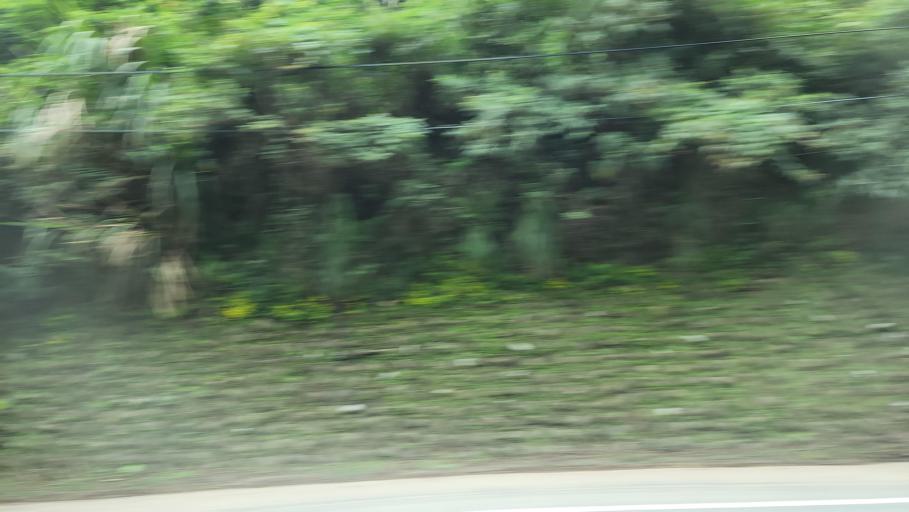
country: TW
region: Taiwan
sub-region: Keelung
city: Keelung
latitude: 25.1626
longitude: 121.6878
